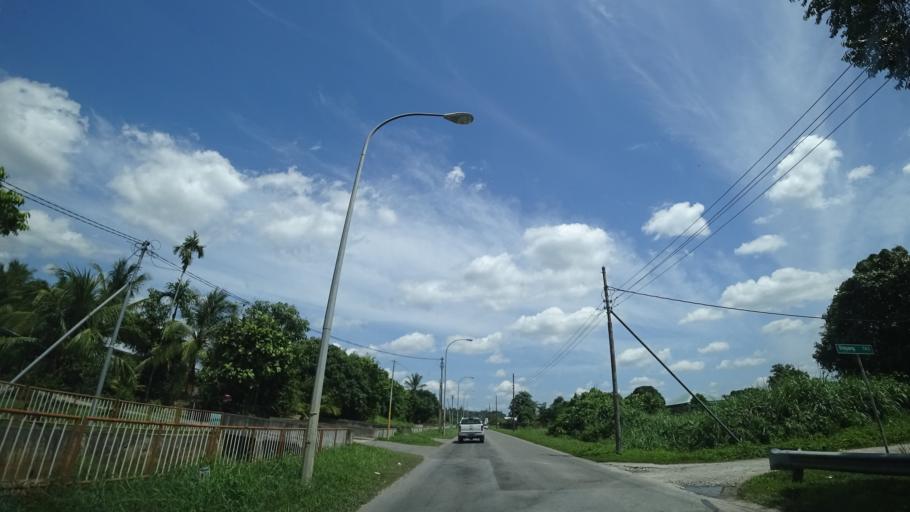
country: BN
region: Brunei and Muara
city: Bandar Seri Begawan
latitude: 4.8691
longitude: 114.8492
